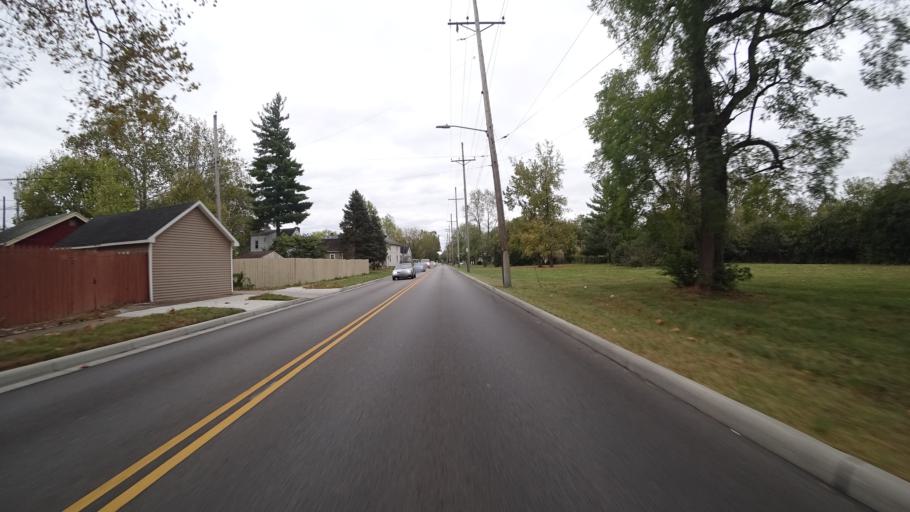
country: US
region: Ohio
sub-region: Butler County
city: Fairfield
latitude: 39.3669
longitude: -84.5633
